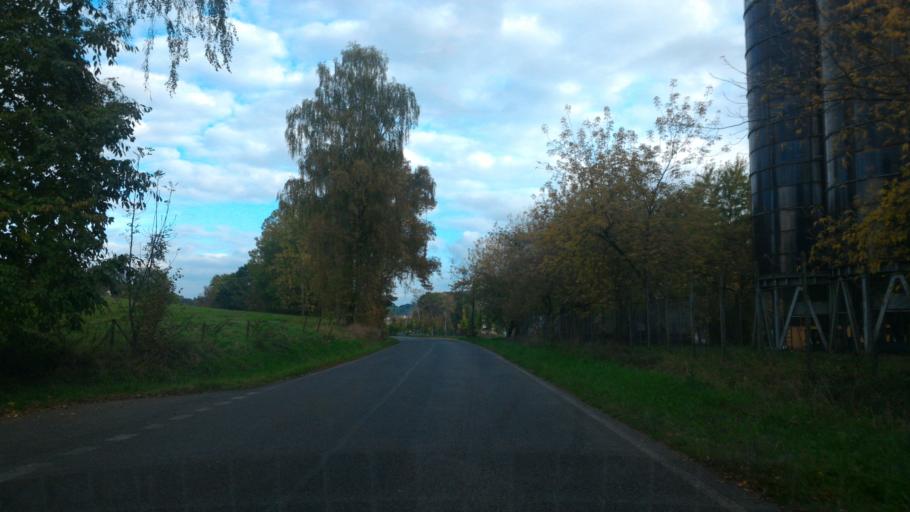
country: CZ
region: Ustecky
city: Ceska Kamenice
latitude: 50.8011
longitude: 14.4013
